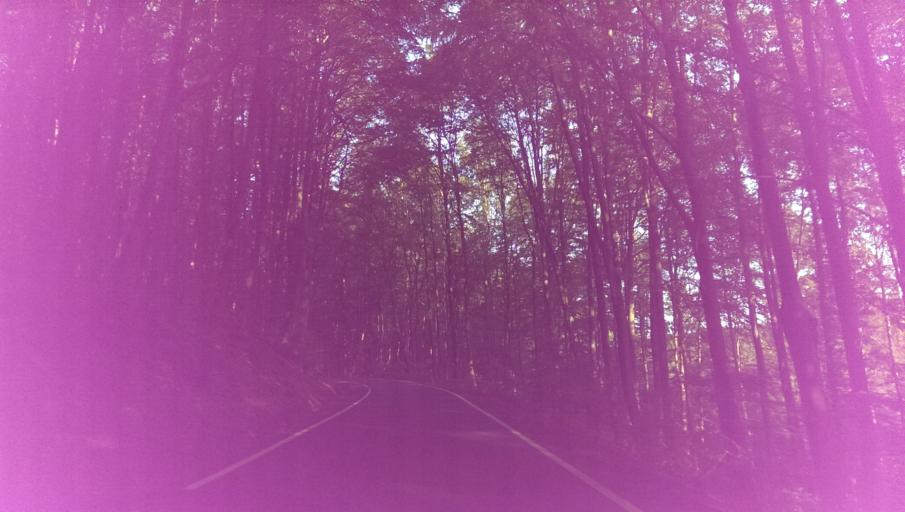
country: CZ
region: South Moravian
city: Zeravice
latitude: 49.0754
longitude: 17.2196
